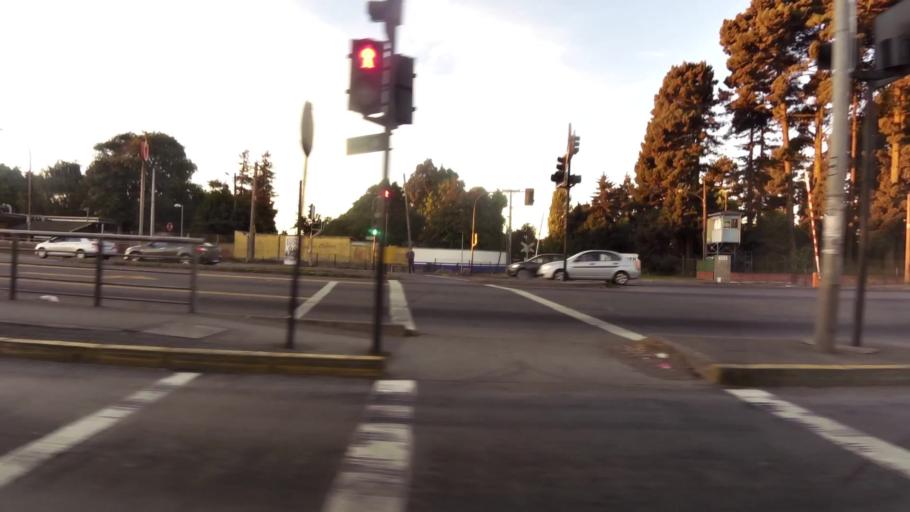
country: CL
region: Biobio
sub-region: Provincia de Concepcion
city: Concepcion
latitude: -36.8388
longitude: -73.0968
